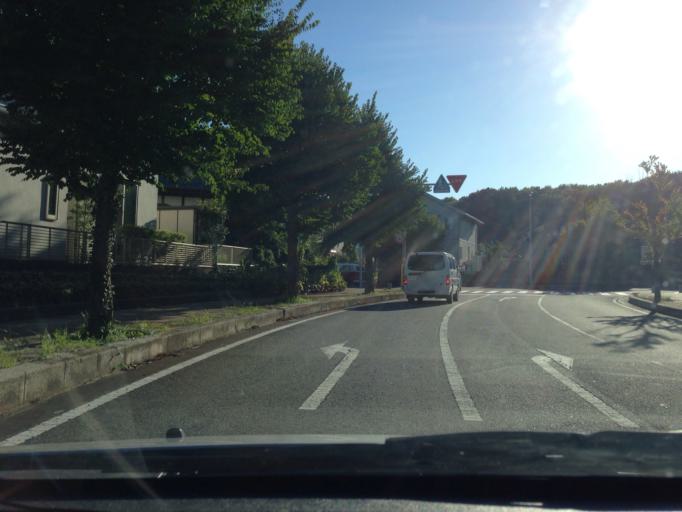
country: JP
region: Ibaraki
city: Naka
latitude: 36.0631
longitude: 140.1725
